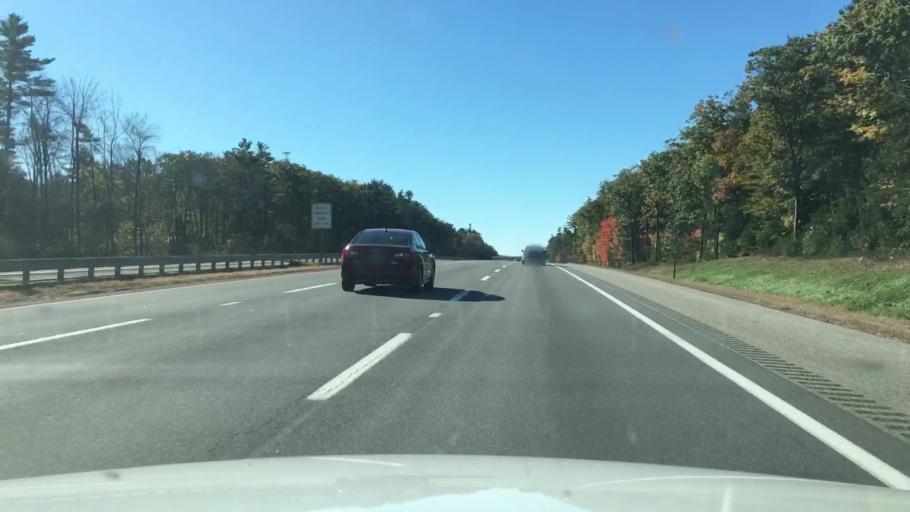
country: US
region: Maine
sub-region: York County
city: West Kennebunk
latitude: 43.3662
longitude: -70.5844
